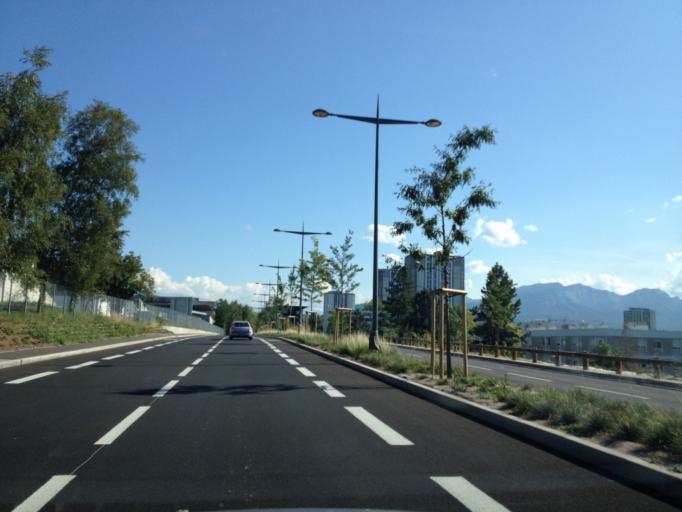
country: FR
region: Rhone-Alpes
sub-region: Departement de la Savoie
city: Sonnaz
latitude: 45.5961
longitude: 5.9172
